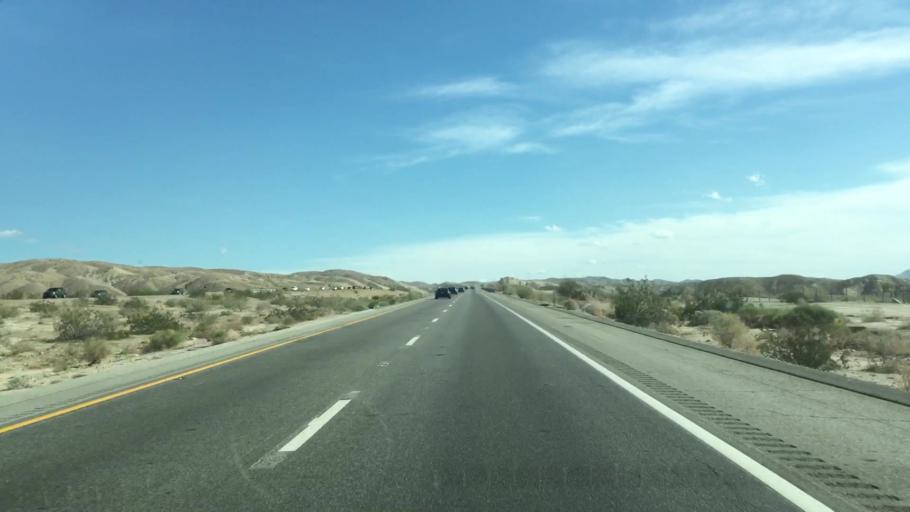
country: US
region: California
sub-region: Riverside County
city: Coachella
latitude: 33.7023
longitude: -116.1261
